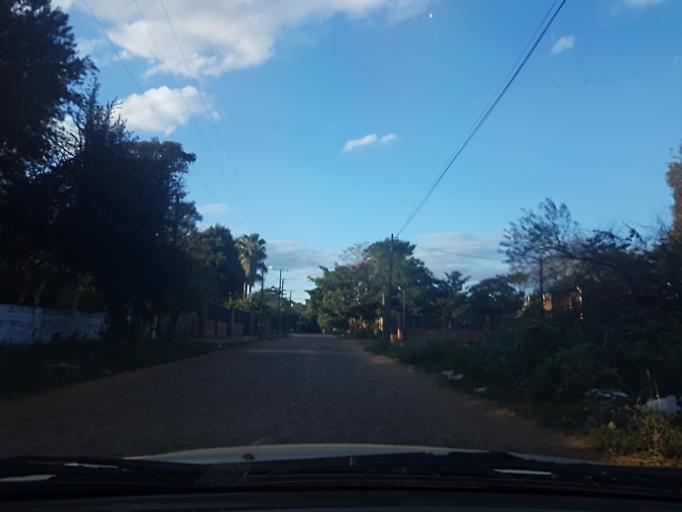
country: PY
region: Central
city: Colonia Mariano Roque Alonso
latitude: -25.2154
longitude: -57.5218
